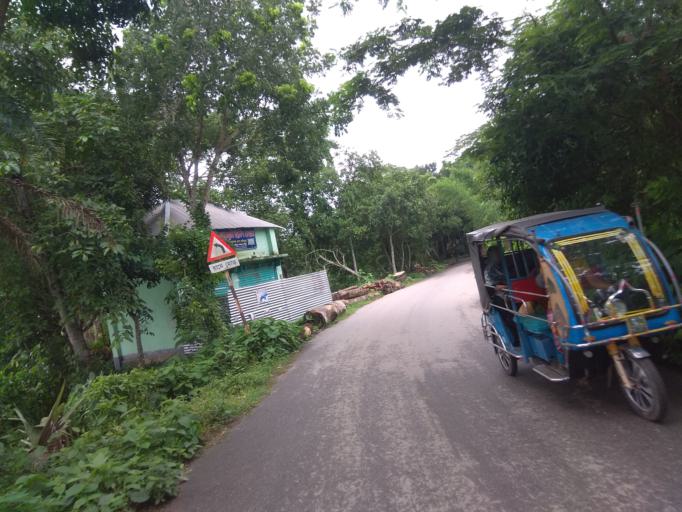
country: BD
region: Dhaka
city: Dohar
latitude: 23.4224
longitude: 90.0647
